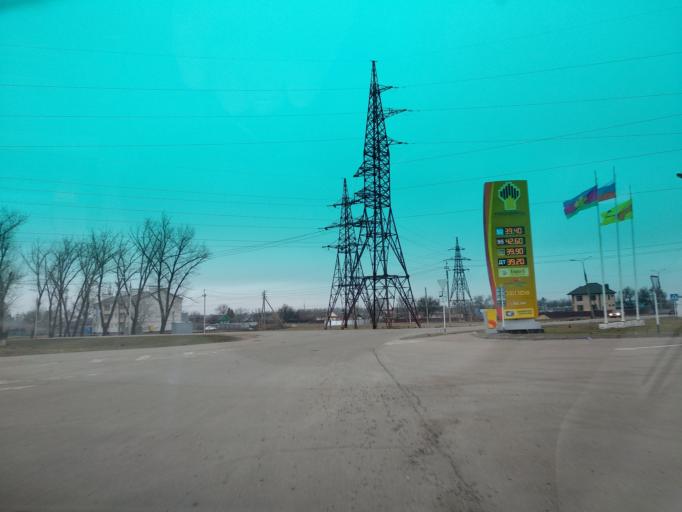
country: RU
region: Krasnodarskiy
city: Tikhoretsk
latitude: 45.8400
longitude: 40.1240
